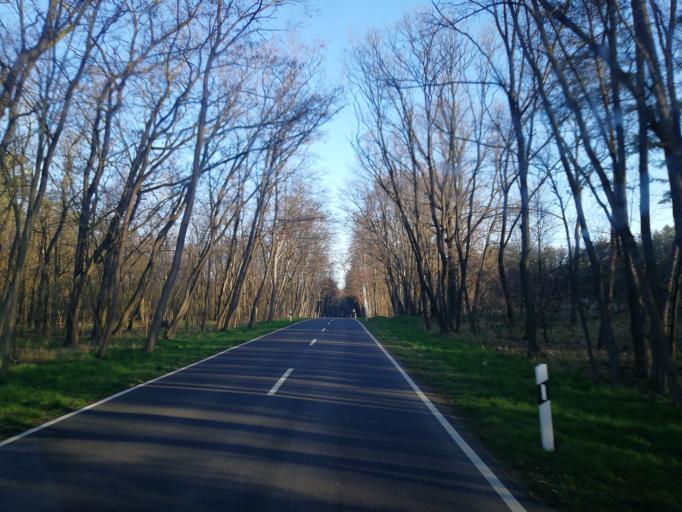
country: DE
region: Brandenburg
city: Drahnsdorf
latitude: 51.8987
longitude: 13.6063
